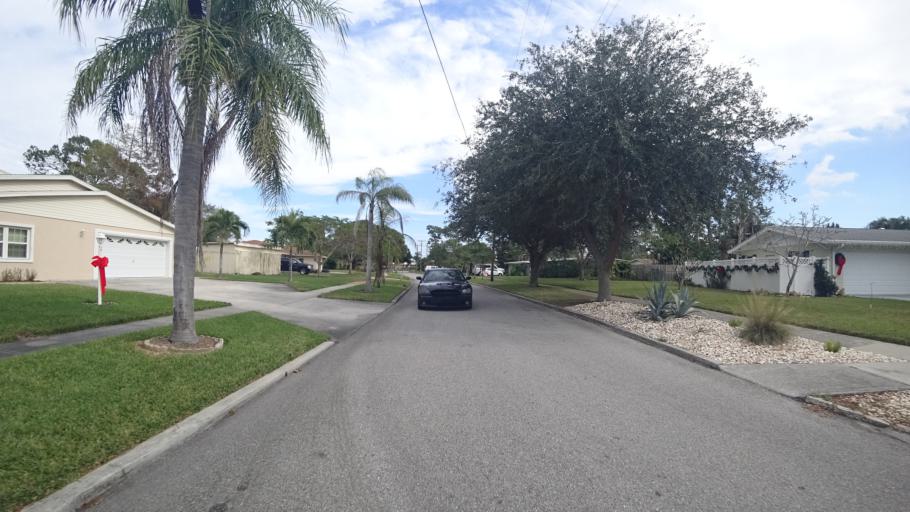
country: US
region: Florida
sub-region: Manatee County
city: West Bradenton
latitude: 27.4919
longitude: -82.6383
